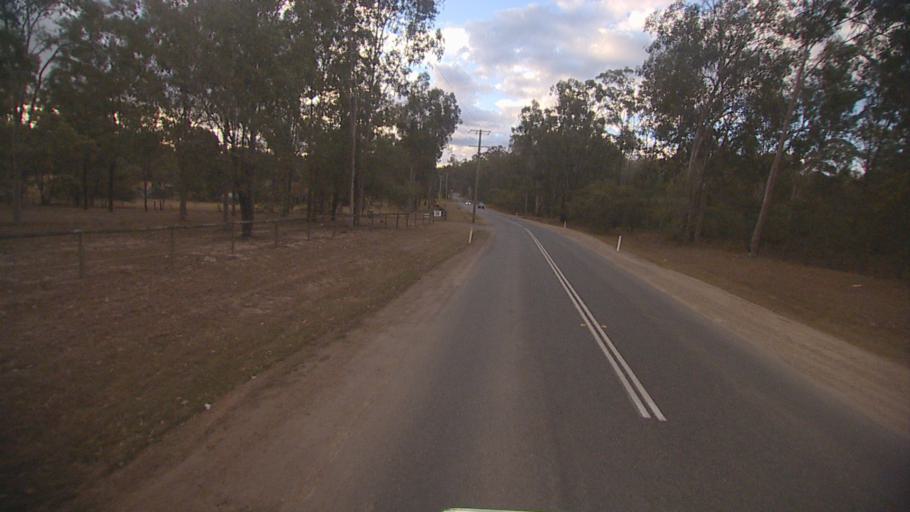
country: AU
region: Queensland
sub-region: Logan
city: Cedar Vale
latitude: -27.8520
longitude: 153.0520
